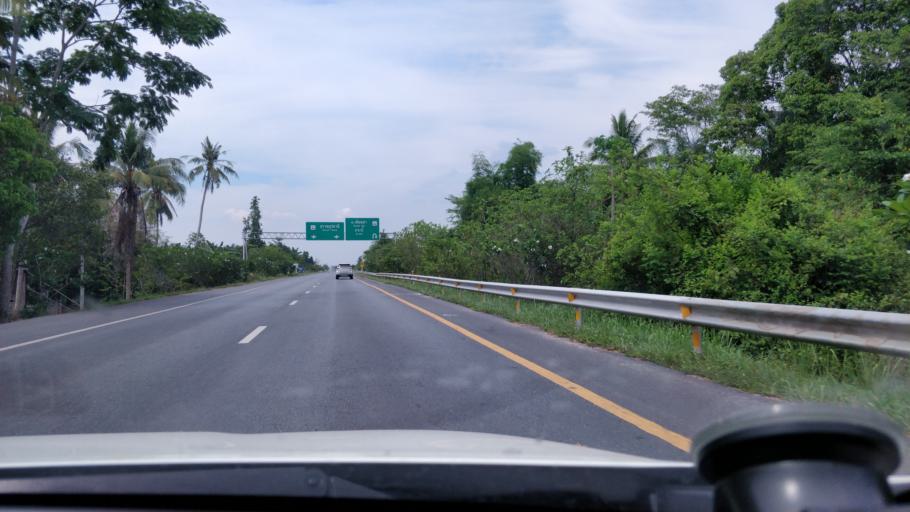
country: TH
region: Surat Thani
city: Khian Sa
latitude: 8.8387
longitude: 99.1763
